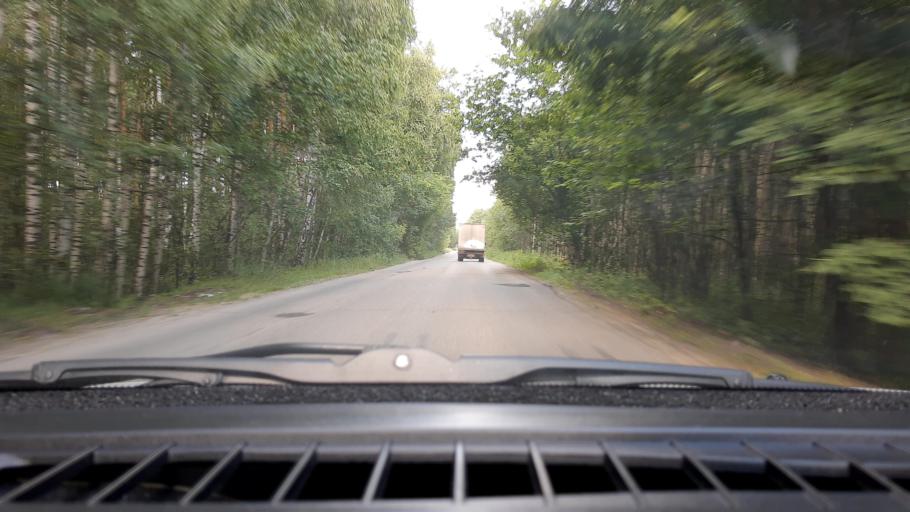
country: RU
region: Nizjnij Novgorod
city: Babino
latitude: 56.3173
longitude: 43.6246
